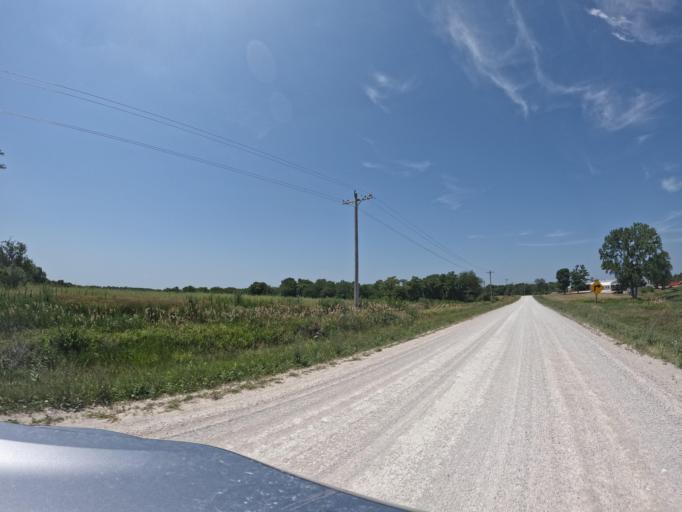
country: US
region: Iowa
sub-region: Henry County
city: Mount Pleasant
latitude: 40.9048
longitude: -91.5431
